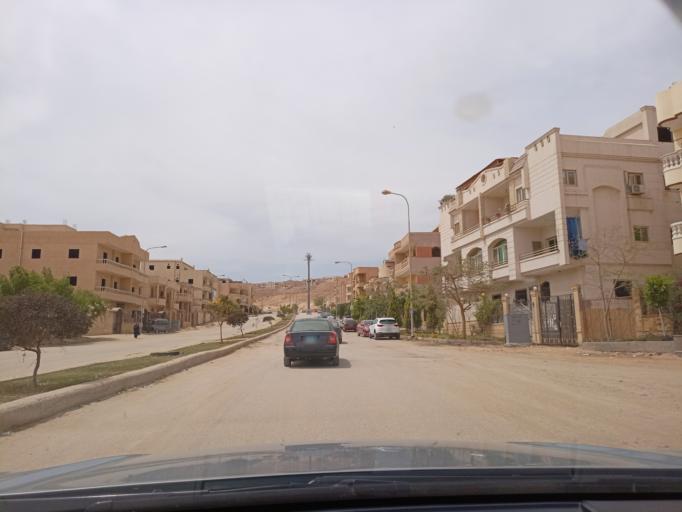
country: EG
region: Muhafazat al Qalyubiyah
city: Al Khankah
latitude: 30.2372
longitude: 31.4891
